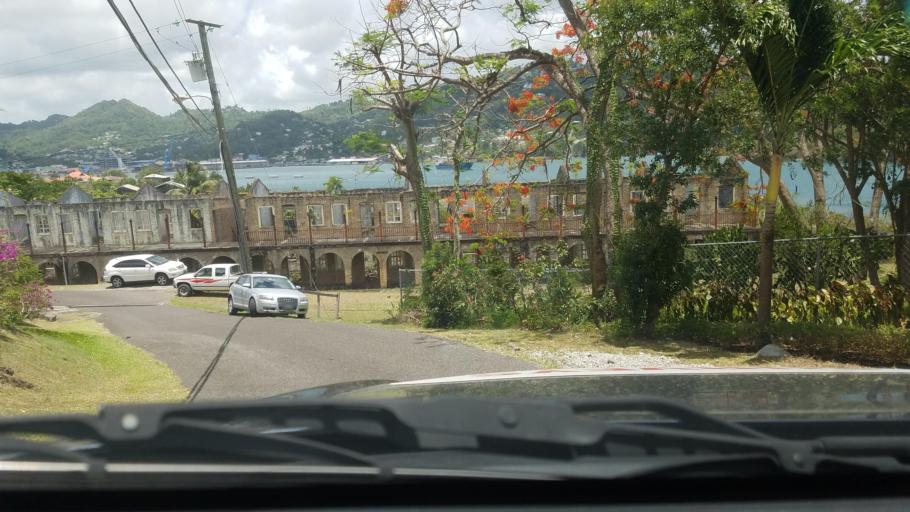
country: LC
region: Castries Quarter
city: Castries
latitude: 14.0198
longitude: -61.0019
